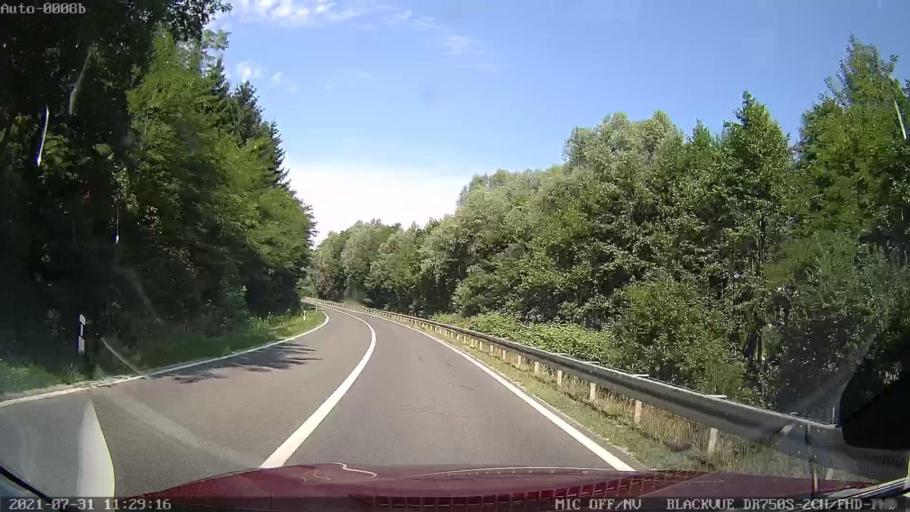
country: HR
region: Varazdinska
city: Ljubescica
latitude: 46.2064
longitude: 16.4197
